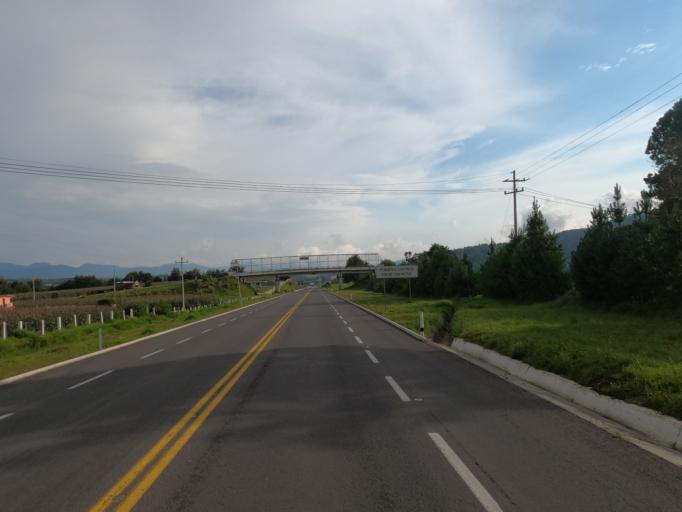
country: MX
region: Mexico
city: Amanalco de Becerra
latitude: 19.3345
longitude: -99.9959
